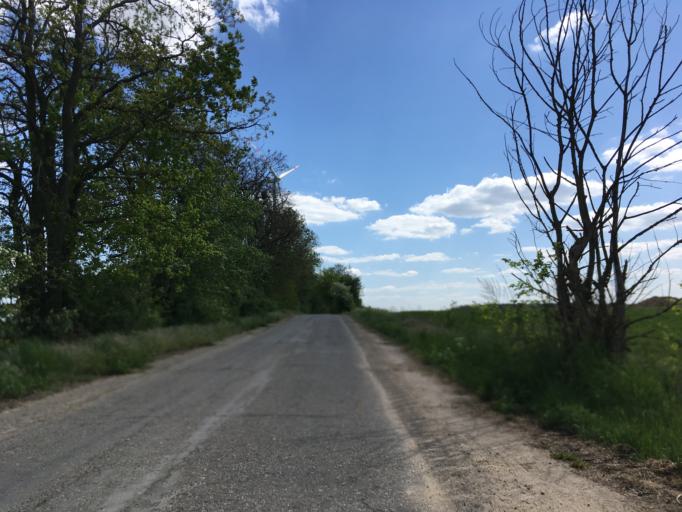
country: DE
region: Brandenburg
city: Rudnitz
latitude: 52.6855
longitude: 13.6715
